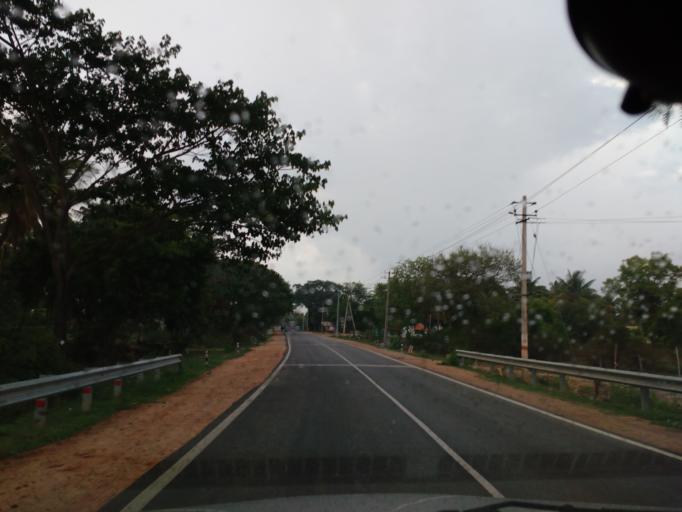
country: IN
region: Karnataka
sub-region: Tumkur
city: Tiptur
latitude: 13.2718
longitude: 76.5129
